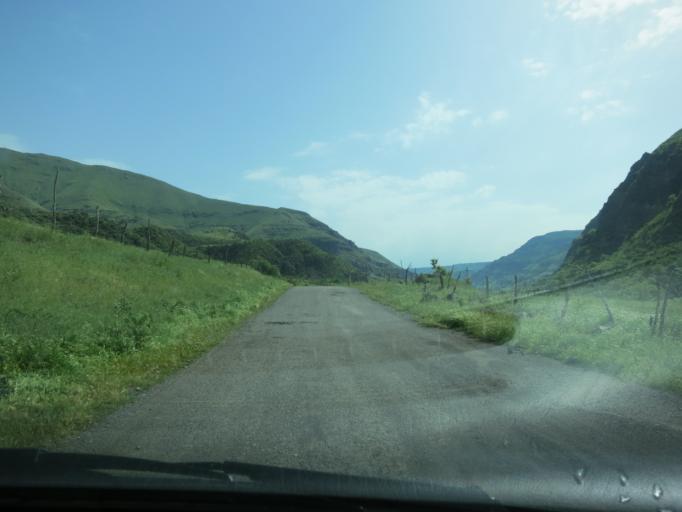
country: TR
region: Ardahan
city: Kurtkale
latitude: 41.3717
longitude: 43.2595
